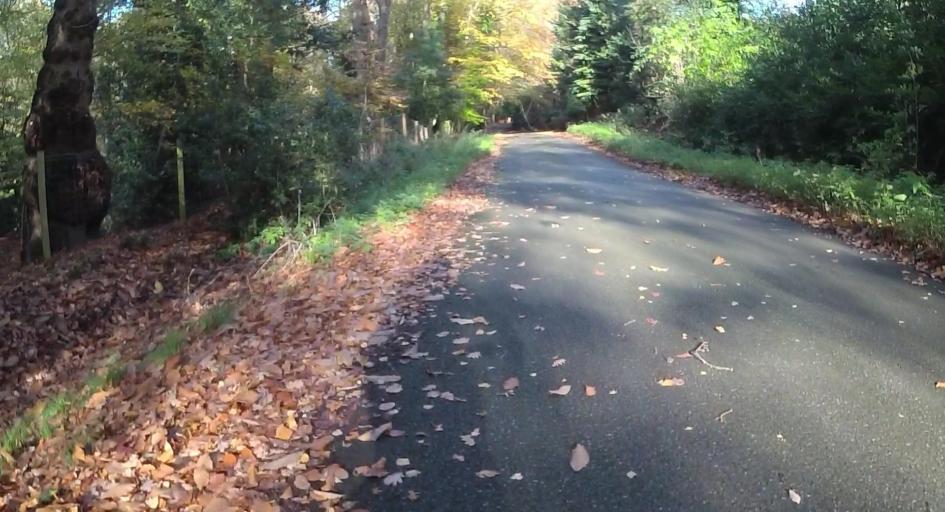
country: GB
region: England
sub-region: West Berkshire
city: Arborfield
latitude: 51.3788
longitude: -0.9273
